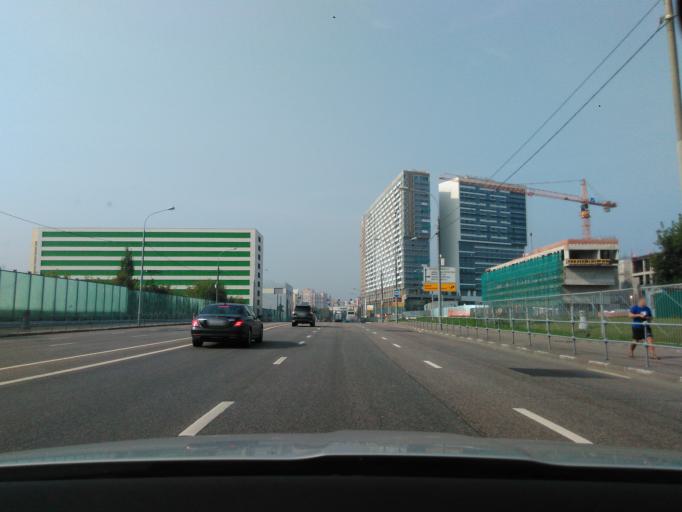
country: RU
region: Moscow
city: Sokol
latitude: 55.7892
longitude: 37.5471
